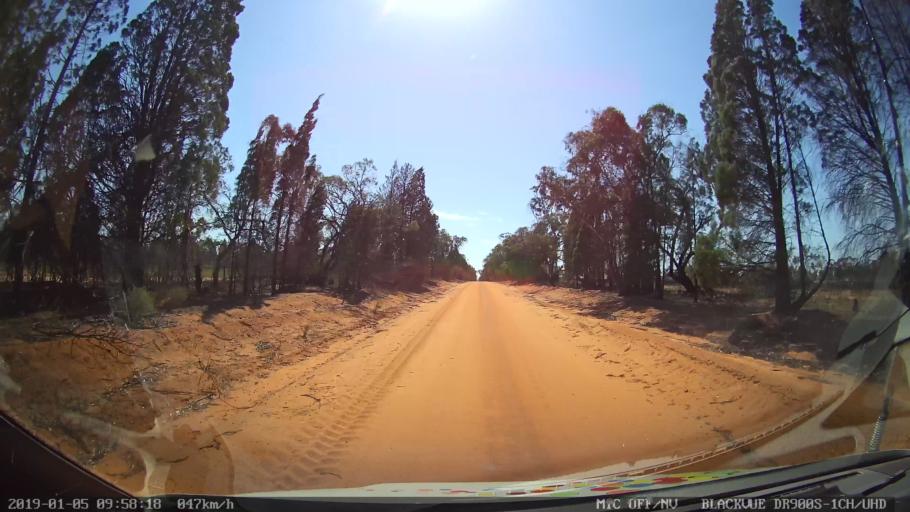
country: AU
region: New South Wales
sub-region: Gilgandra
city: Gilgandra
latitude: -31.6664
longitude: 148.8082
